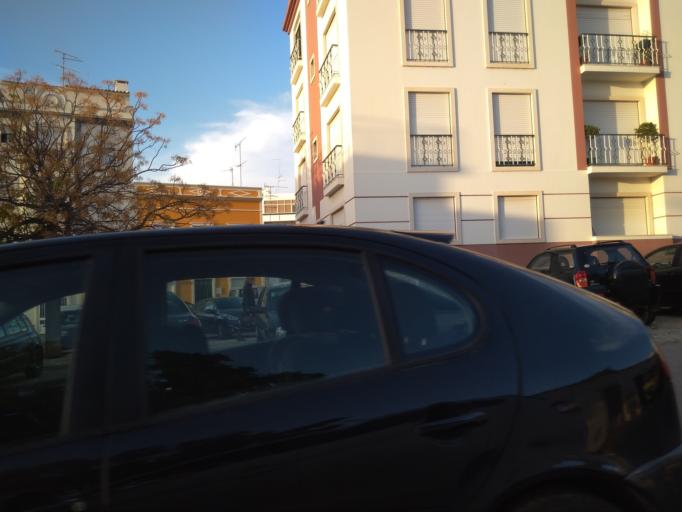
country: PT
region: Faro
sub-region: Faro
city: Faro
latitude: 37.0205
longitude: -7.9363
